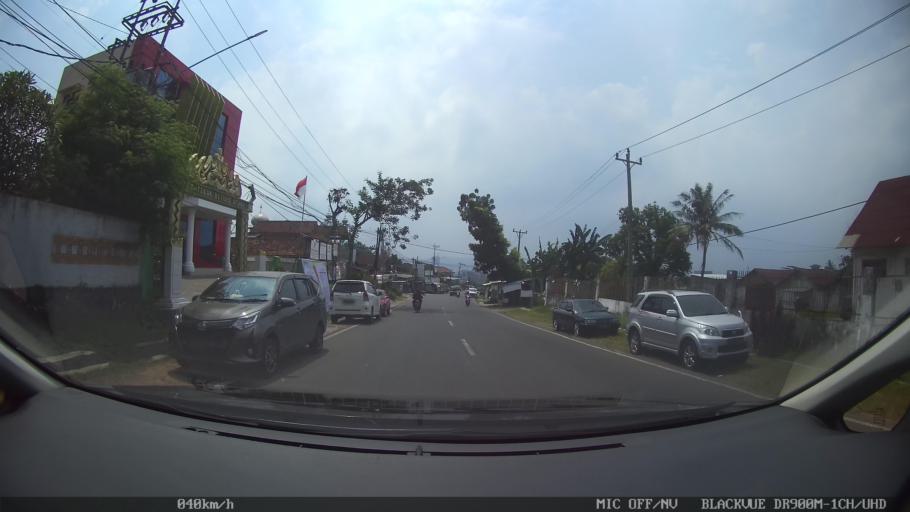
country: ID
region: Lampung
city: Bandarlampung
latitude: -5.4395
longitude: 105.2620
